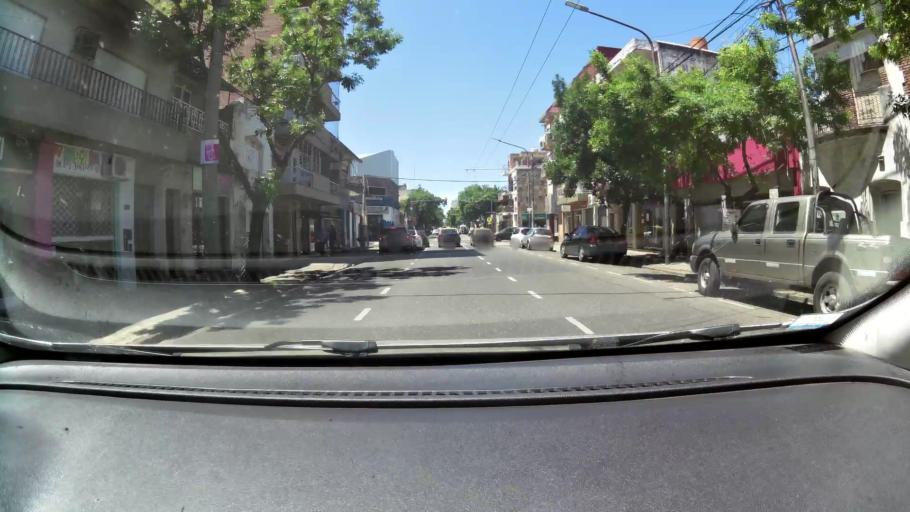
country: AR
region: Santa Fe
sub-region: Departamento de Rosario
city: Rosario
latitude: -32.9435
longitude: -60.6850
